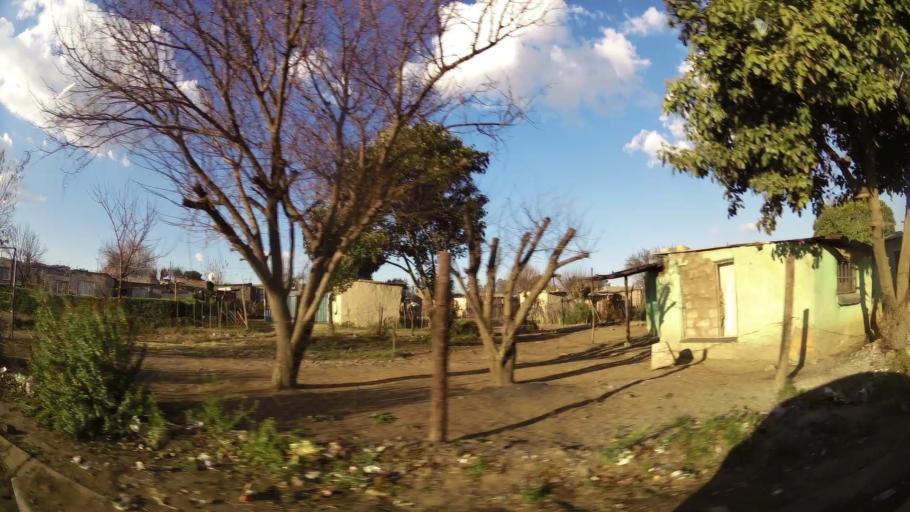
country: ZA
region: Mpumalanga
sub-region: Nkangala District Municipality
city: Witbank
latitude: -25.8759
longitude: 29.1989
